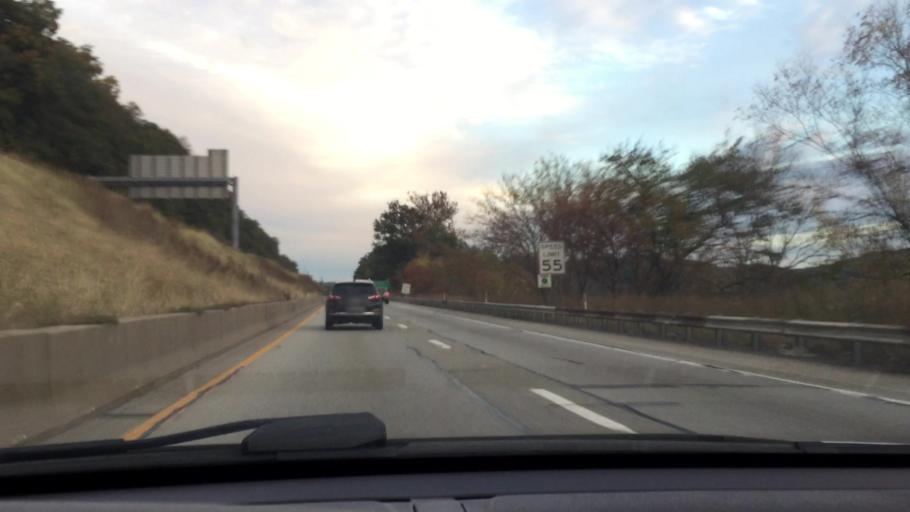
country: US
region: Pennsylvania
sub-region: Allegheny County
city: Aspinwall
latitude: 40.4918
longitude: -79.8926
